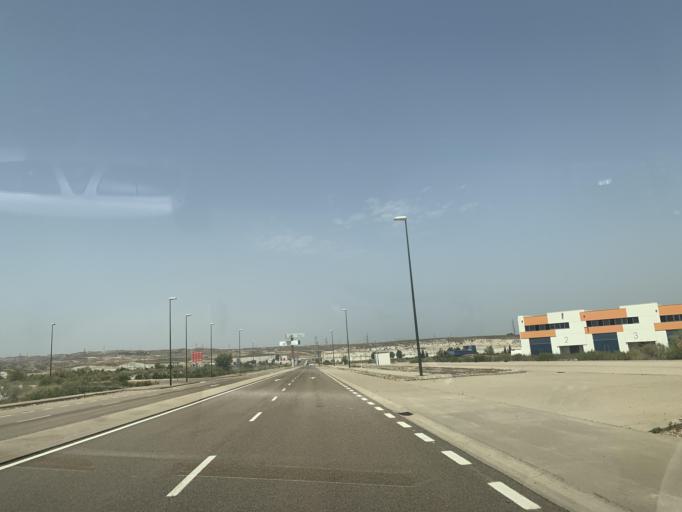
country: ES
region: Aragon
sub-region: Provincia de Zaragoza
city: Zaragoza
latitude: 41.5850
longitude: -0.8335
